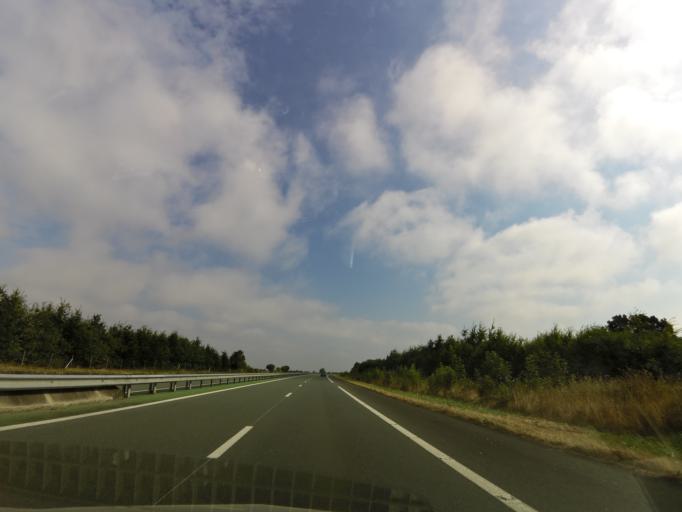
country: FR
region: Pays de la Loire
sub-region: Departement de la Vendee
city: La Ferriere
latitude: 46.7292
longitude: -1.2760
